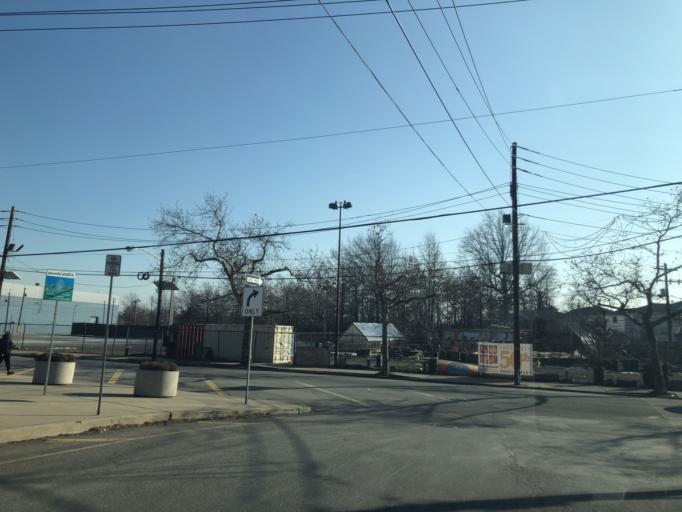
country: US
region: New Jersey
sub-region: Hudson County
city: Harrison
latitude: 40.7300
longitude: -74.1466
